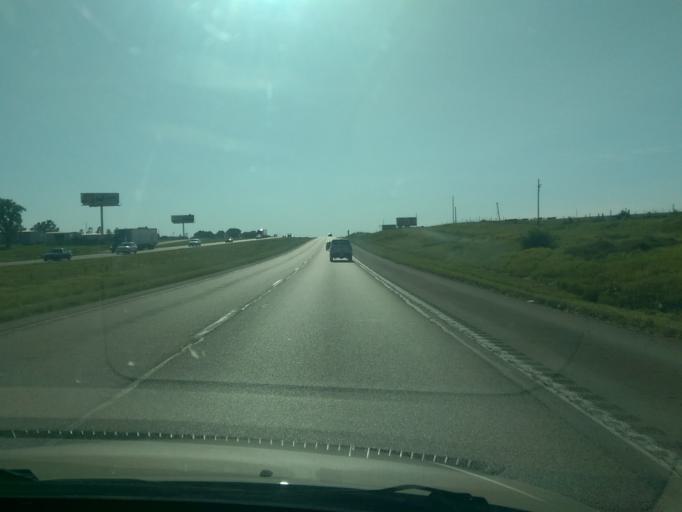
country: US
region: Missouri
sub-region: Lafayette County
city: Odessa
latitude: 39.0098
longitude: -94.0112
